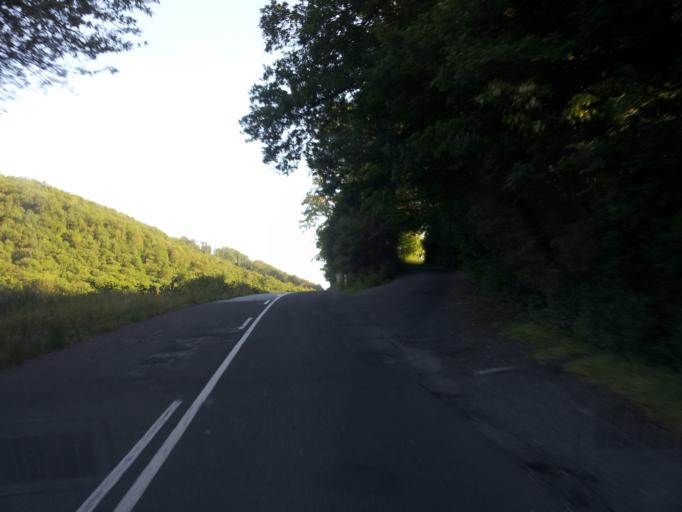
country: SK
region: Banskobystricky
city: Svaety Anton
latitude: 48.3988
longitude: 18.9374
